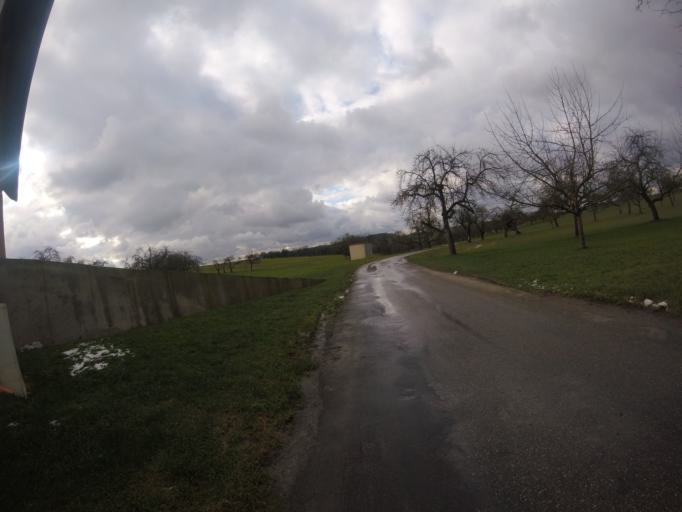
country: DE
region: Baden-Wuerttemberg
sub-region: Regierungsbezirk Stuttgart
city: Aspach
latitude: 48.9584
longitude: 9.4010
